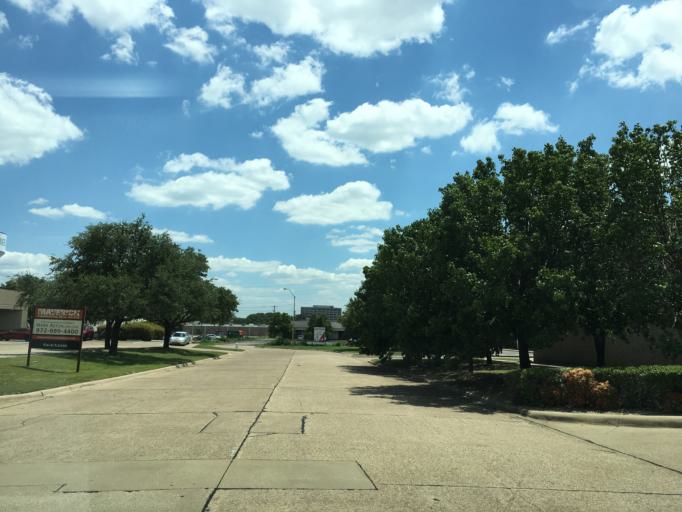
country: US
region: Texas
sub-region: Dallas County
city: Addison
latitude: 32.9490
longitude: -96.8368
